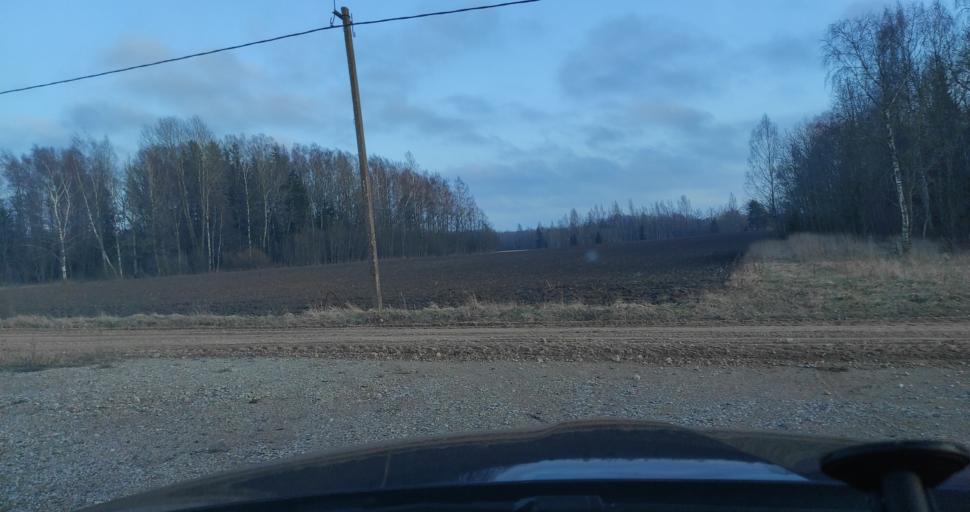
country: LV
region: Aizpute
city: Aizpute
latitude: 56.7990
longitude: 21.7952
